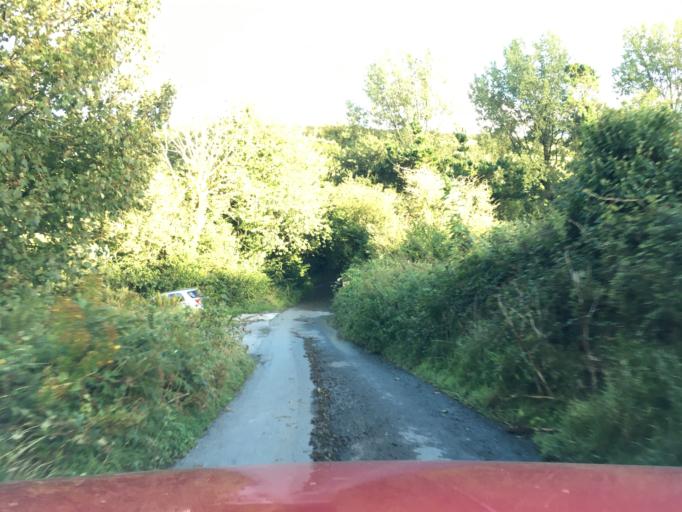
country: GB
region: England
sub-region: Devon
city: Dartmouth
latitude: 50.3373
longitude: -3.6031
